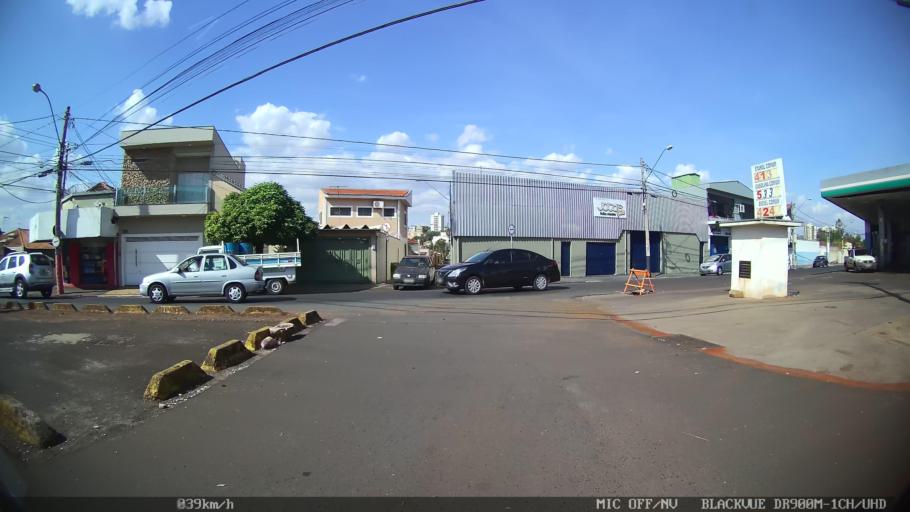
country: BR
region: Sao Paulo
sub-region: Ribeirao Preto
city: Ribeirao Preto
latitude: -21.1825
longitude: -47.8227
